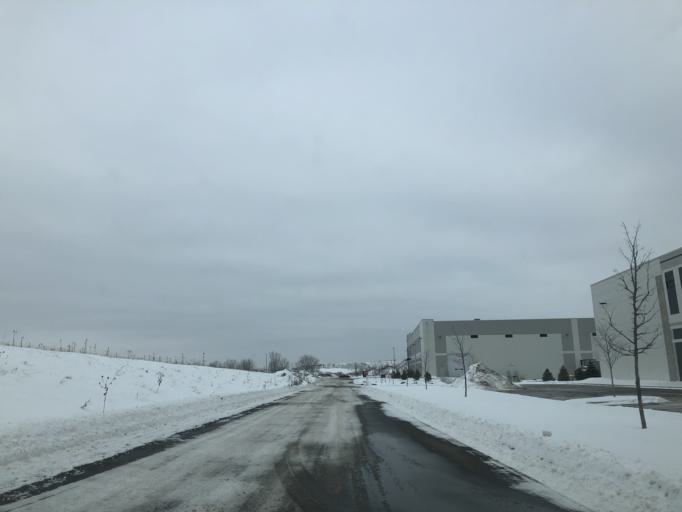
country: US
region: Minnesota
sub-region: Hennepin County
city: Osseo
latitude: 45.0925
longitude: -93.4168
